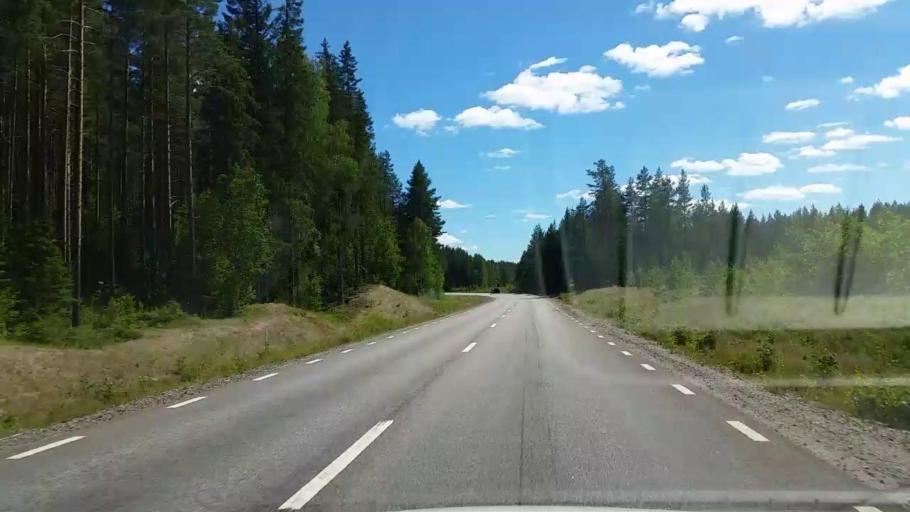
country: SE
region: Gaevleborg
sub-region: Ovanakers Kommun
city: Edsbyn
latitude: 61.1804
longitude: 15.8792
